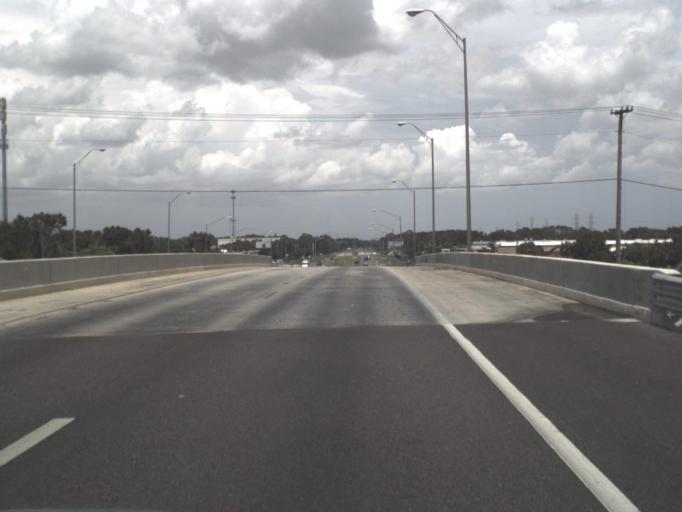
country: US
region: Florida
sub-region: Hillsborough County
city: East Lake-Orient Park
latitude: 27.9671
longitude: -82.3603
